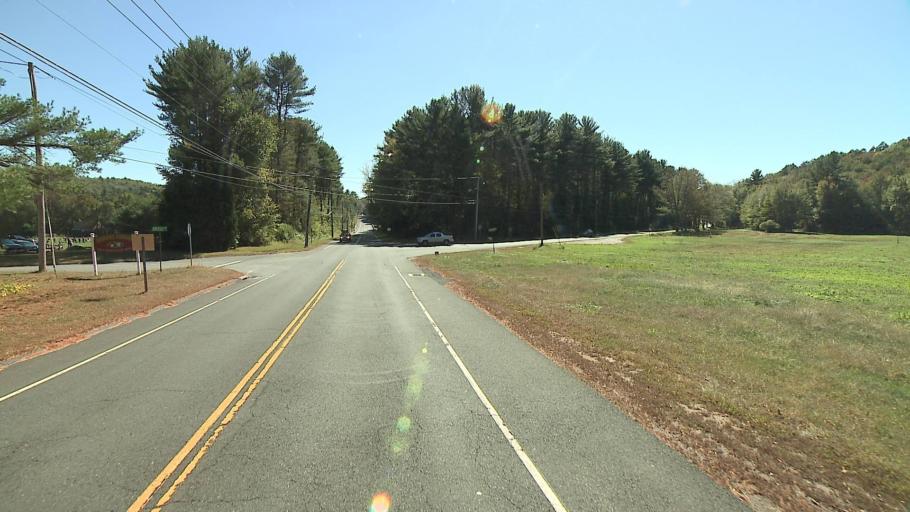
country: US
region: Connecticut
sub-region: Litchfield County
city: New Hartford Center
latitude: 41.8283
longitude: -72.9771
